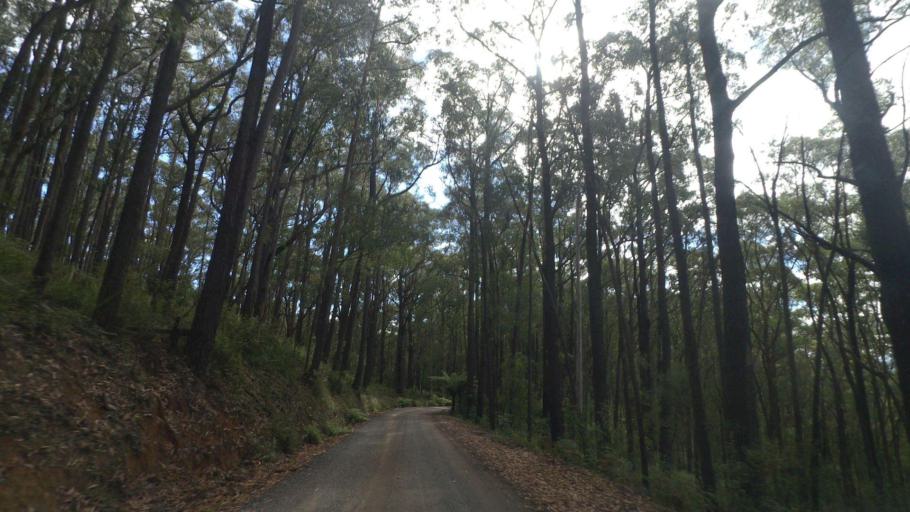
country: AU
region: Victoria
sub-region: Cardinia
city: Gembrook
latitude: -37.9184
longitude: 145.6087
